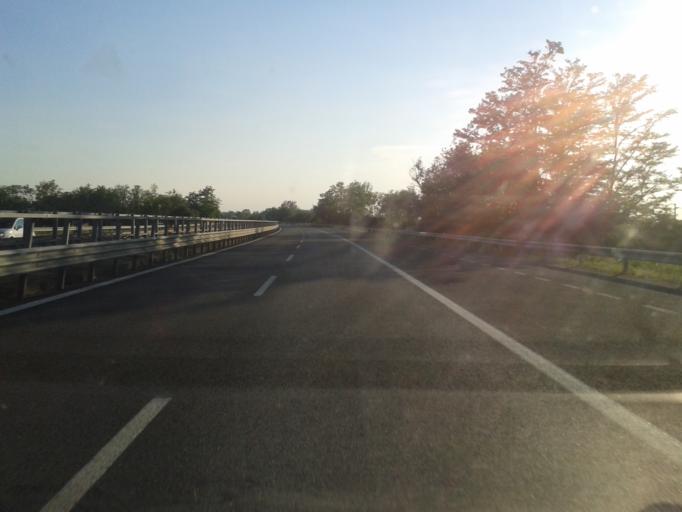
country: IT
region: Piedmont
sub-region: Provincia di Alessandria
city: Fresonara
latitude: 44.7753
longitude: 8.6759
